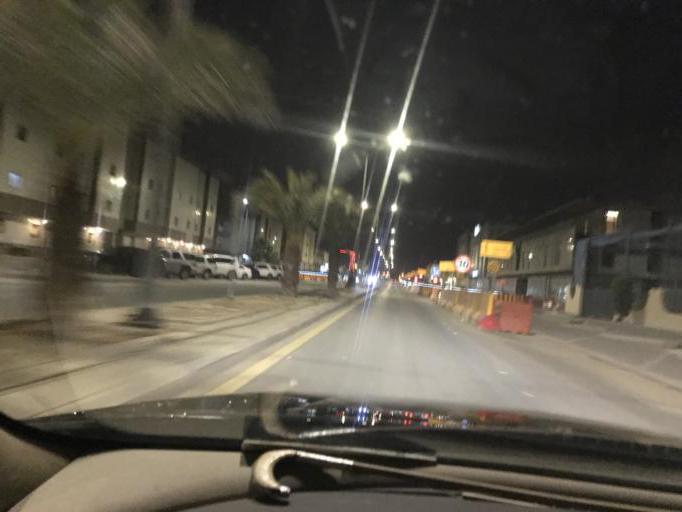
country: SA
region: Ar Riyad
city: Riyadh
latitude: 24.7997
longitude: 46.7083
